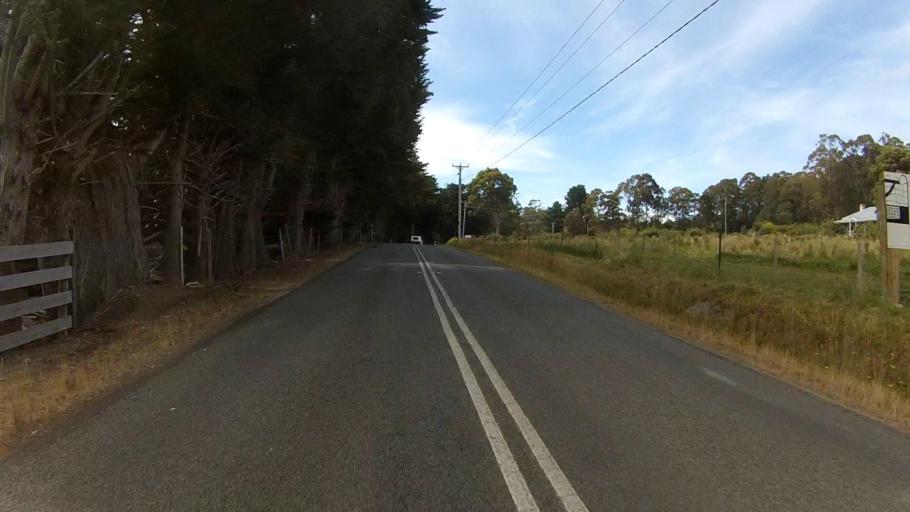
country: AU
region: Tasmania
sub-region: Kingborough
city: Kettering
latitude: -43.1879
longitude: 147.2439
